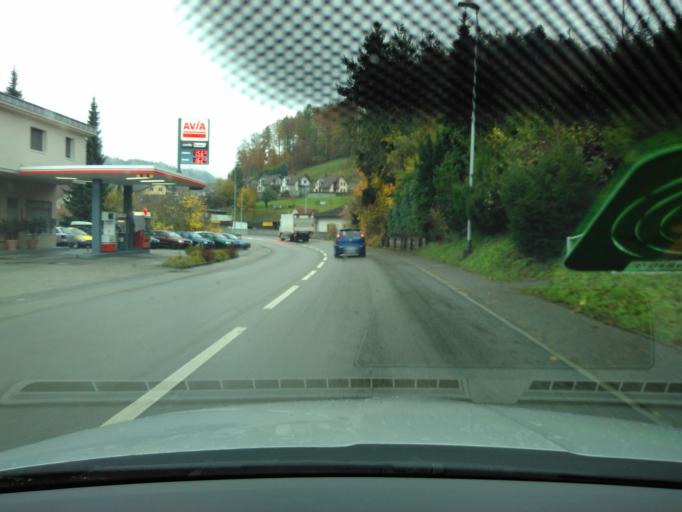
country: CH
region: Aargau
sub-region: Bezirk Zofingen
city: Kirchleerau
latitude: 47.2683
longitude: 8.0638
